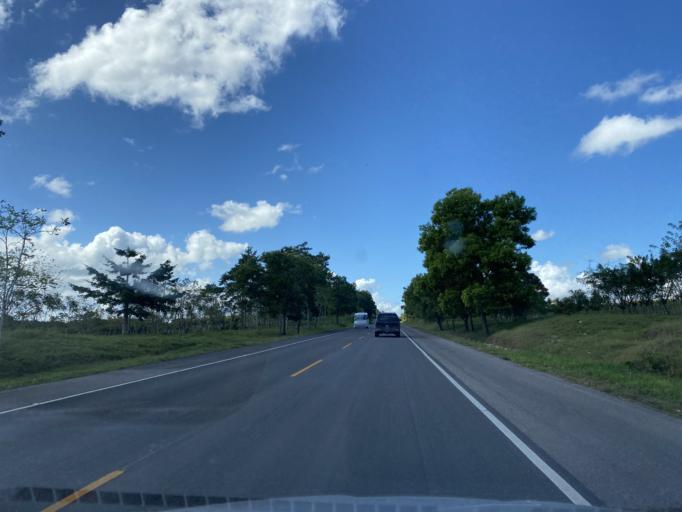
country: DO
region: Monte Plata
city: Sabana Grande de Boya
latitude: 18.9762
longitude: -69.7925
